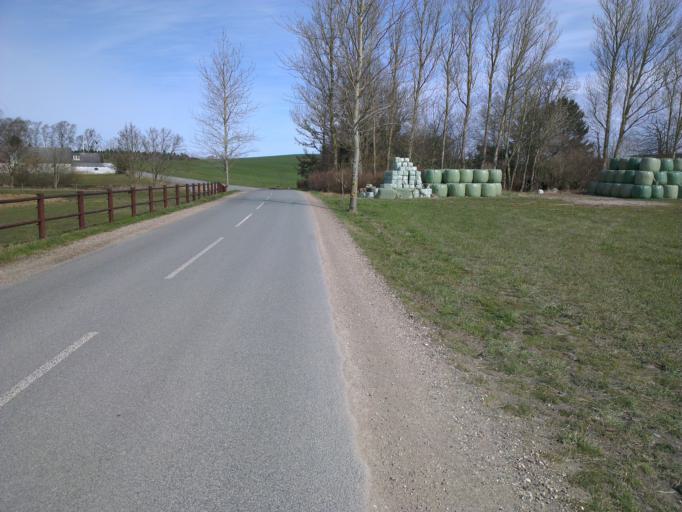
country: DK
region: Capital Region
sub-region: Egedal Kommune
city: Olstykke
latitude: 55.8422
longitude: 12.1250
